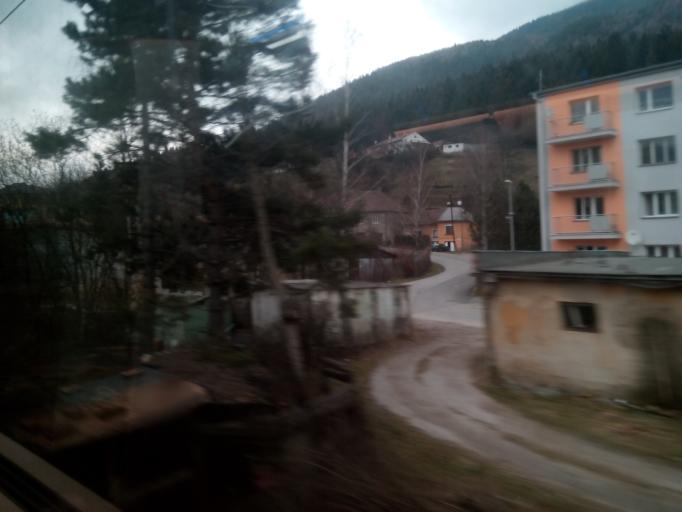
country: SK
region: Zilinsky
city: Ruzomberok
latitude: 49.0879
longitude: 19.2764
